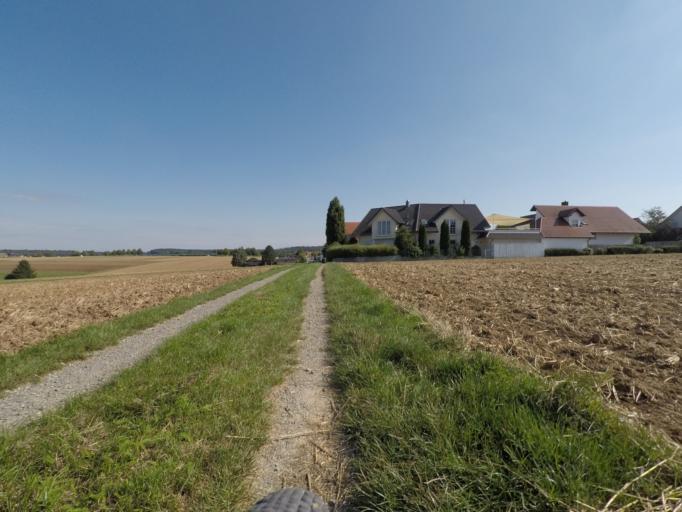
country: DE
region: Baden-Wuerttemberg
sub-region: Regierungsbezirk Stuttgart
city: Hildrizhausen
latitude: 48.6298
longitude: 8.9759
